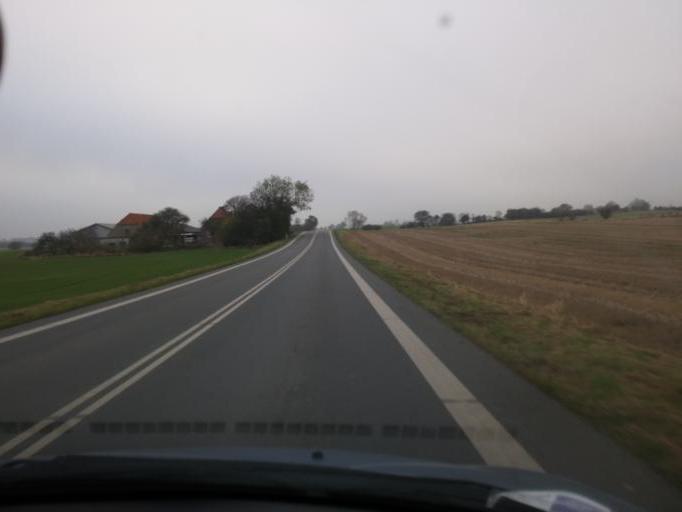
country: DK
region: South Denmark
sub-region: Kerteminde Kommune
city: Kerteminde
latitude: 55.4674
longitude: 10.6769
